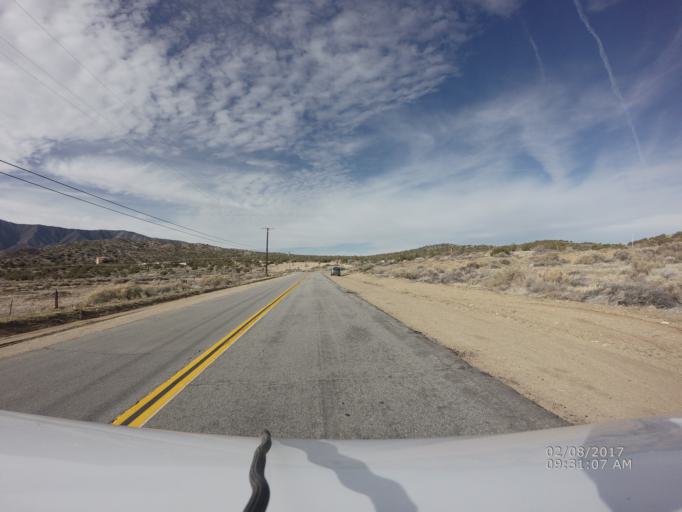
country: US
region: California
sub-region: Los Angeles County
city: Littlerock
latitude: 34.4574
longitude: -117.9002
